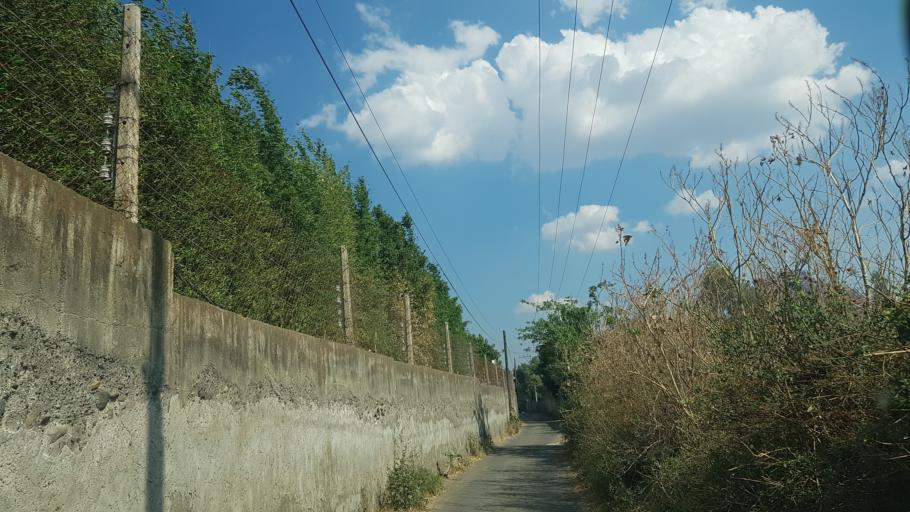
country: MX
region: Puebla
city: Atlixco
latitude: 18.8732
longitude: -98.4853
